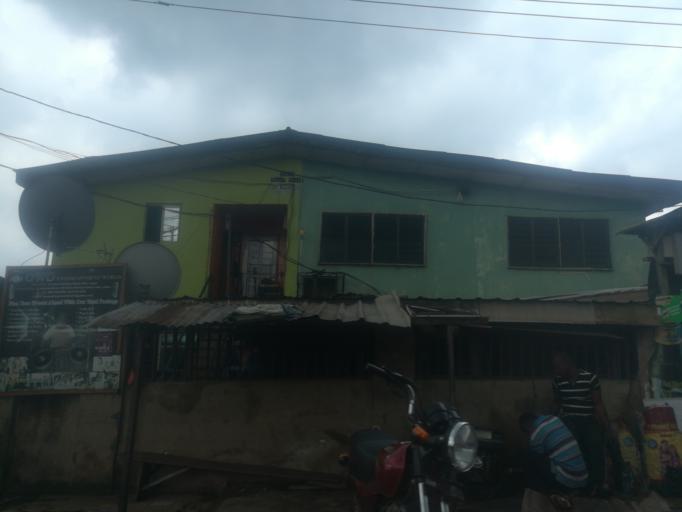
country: NG
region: Lagos
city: Ojota
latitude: 6.5957
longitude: 3.3861
